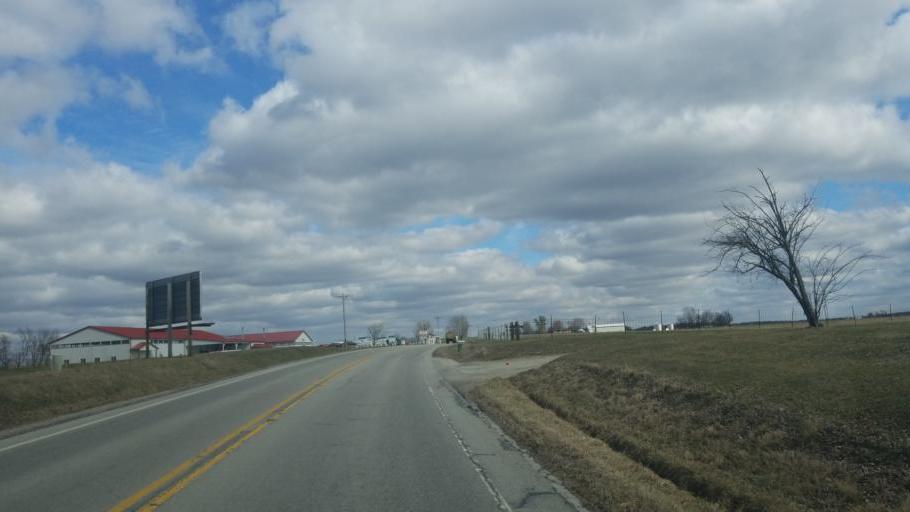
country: US
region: Indiana
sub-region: Parke County
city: Rockville
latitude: 39.7593
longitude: -87.1255
